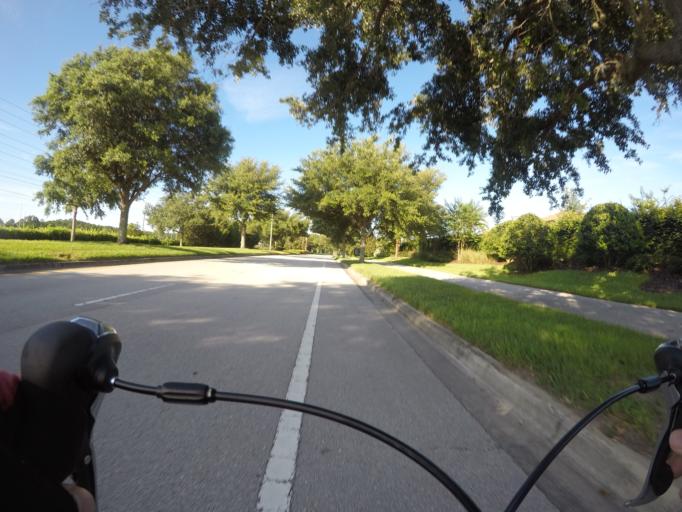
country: US
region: Florida
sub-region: Orange County
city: Meadow Woods
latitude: 28.3975
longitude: -81.2516
